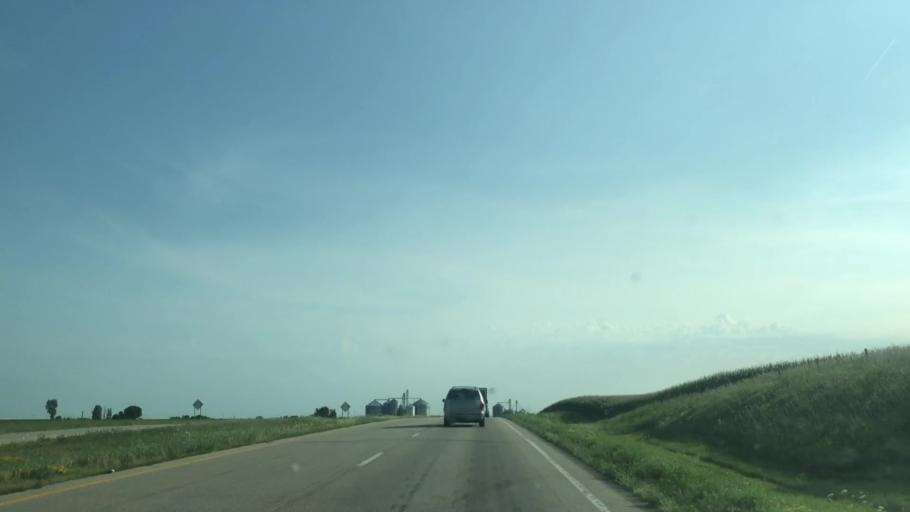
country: US
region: Iowa
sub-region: Marshall County
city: Marshalltown
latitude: 42.0162
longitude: -93.0140
